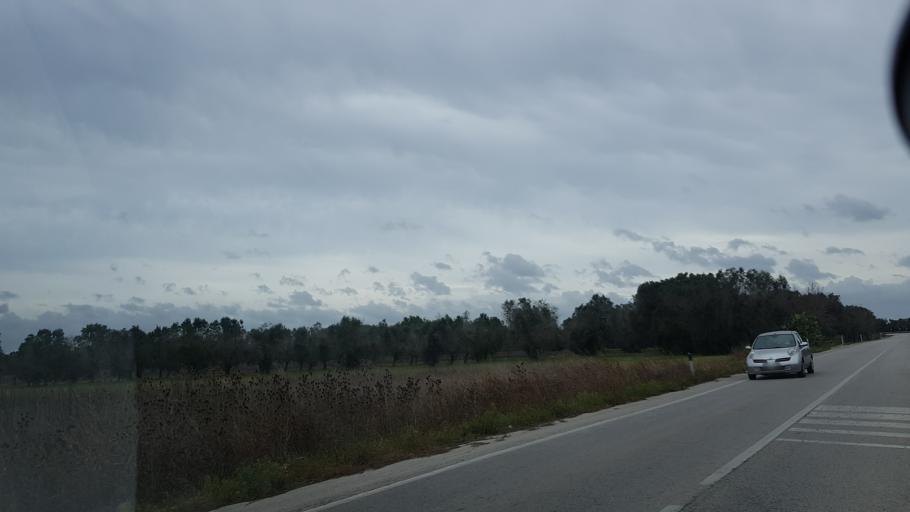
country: IT
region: Apulia
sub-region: Provincia di Lecce
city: Guagnano
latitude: 40.3994
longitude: 17.9187
